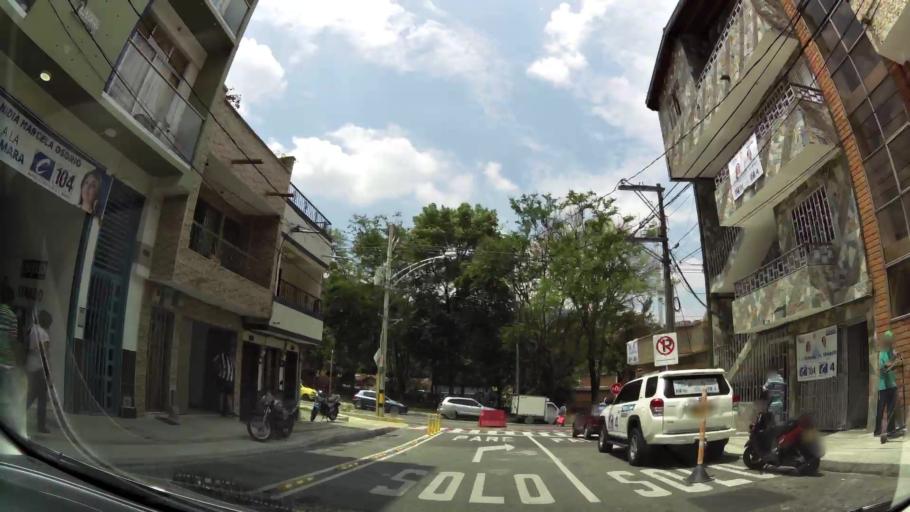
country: CO
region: Antioquia
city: Itagui
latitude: 6.1742
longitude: -75.6098
